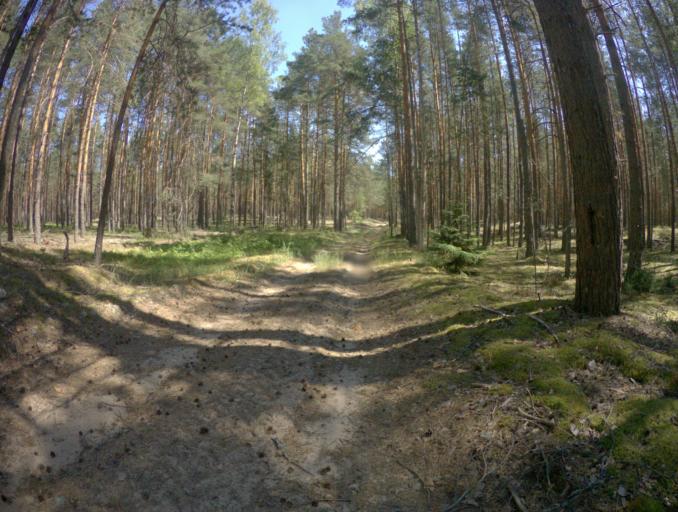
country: RU
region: Ivanovo
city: Talitsy
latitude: 56.3699
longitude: 42.3279
